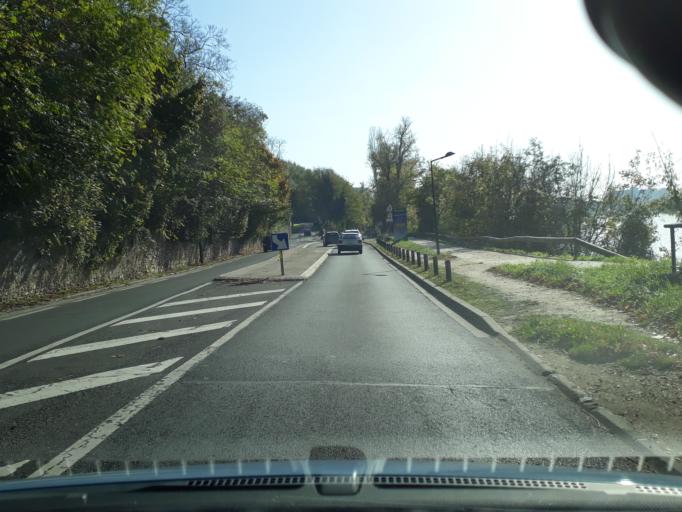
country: FR
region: Ile-de-France
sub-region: Departement de Seine-et-Marne
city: Melun
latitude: 48.5324
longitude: 2.6677
